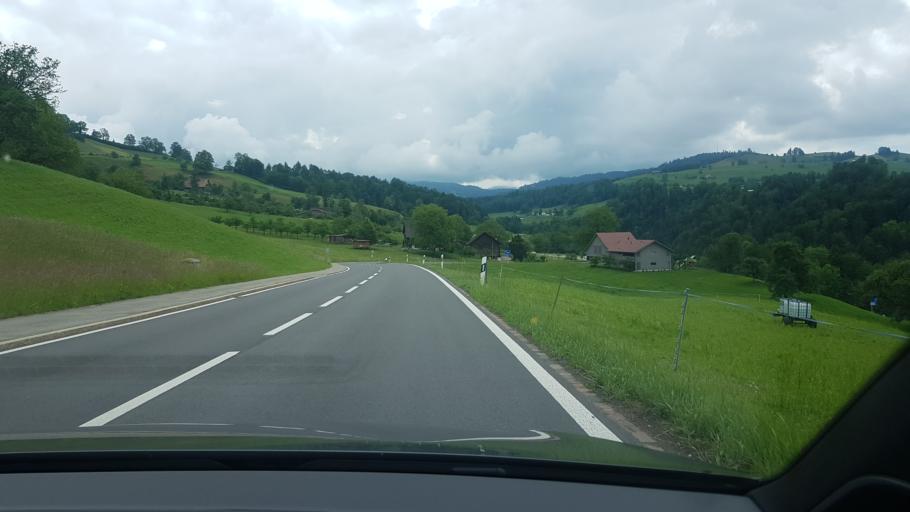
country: CH
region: Zug
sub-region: Zug
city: Menzingen
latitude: 47.1755
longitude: 8.5643
